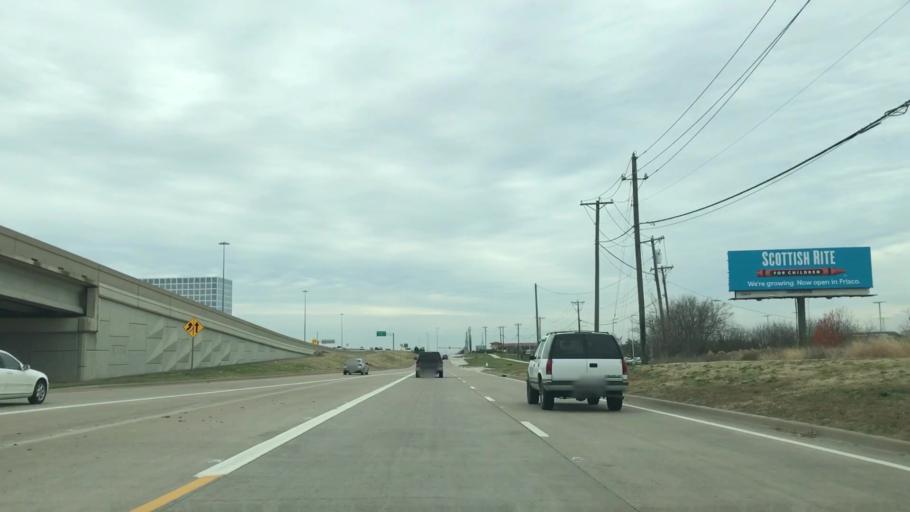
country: US
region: Texas
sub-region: Denton County
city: The Colony
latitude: 33.0894
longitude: -96.8310
